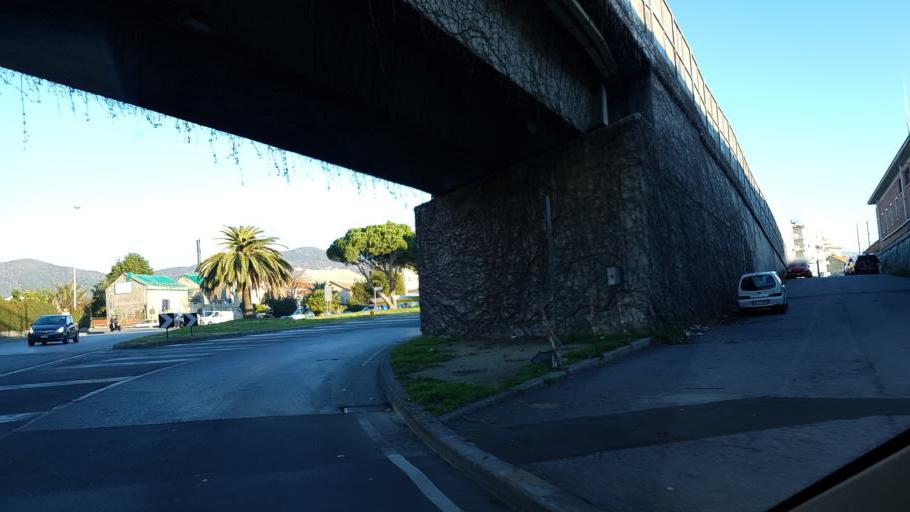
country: IT
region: Liguria
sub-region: Provincia di Savona
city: Valleggia
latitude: 44.2929
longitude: 8.4529
